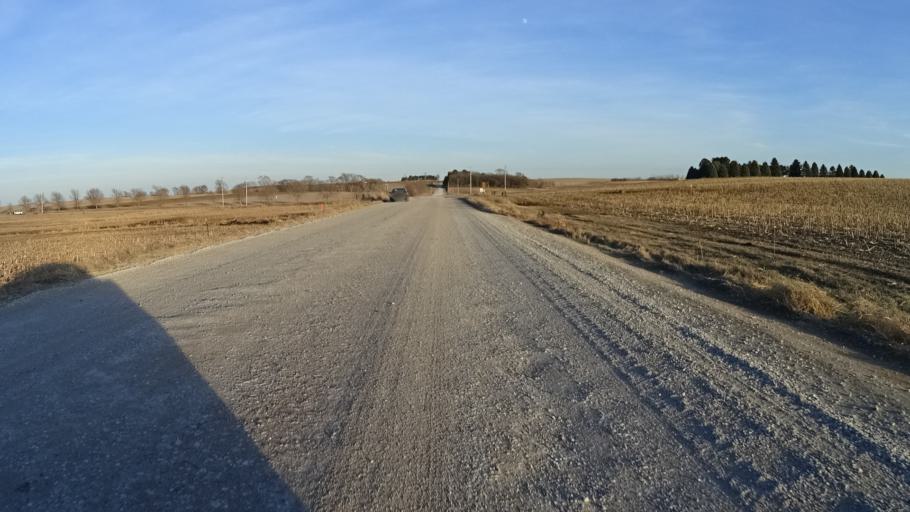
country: US
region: Nebraska
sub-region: Sarpy County
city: Springfield
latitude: 41.1325
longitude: -96.1221
